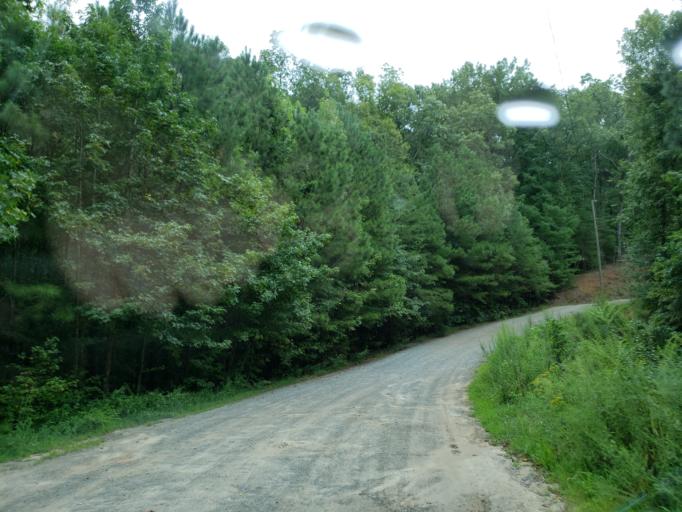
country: US
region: Georgia
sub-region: Gilmer County
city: Ellijay
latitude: 34.5720
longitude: -84.5243
